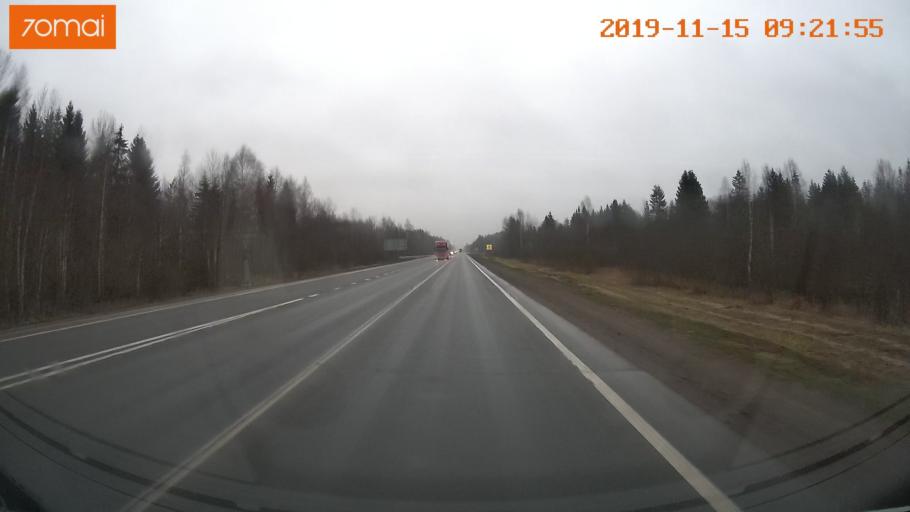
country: RU
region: Vologda
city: Tonshalovo
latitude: 59.2961
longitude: 38.0763
